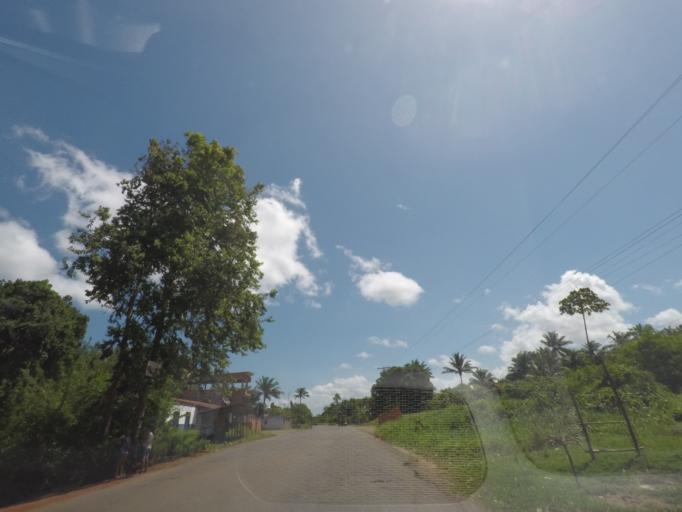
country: BR
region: Bahia
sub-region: Valenca
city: Valenca
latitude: -13.3911
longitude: -39.0755
